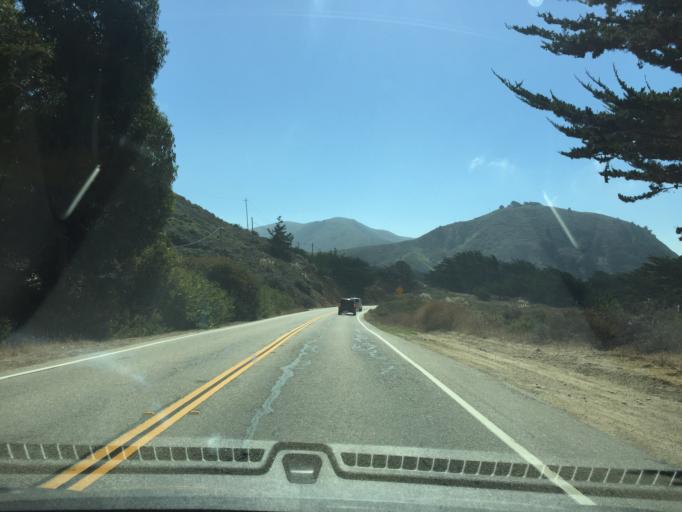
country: US
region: California
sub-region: Monterey County
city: Carmel-by-the-Sea
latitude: 36.3852
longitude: -121.9004
